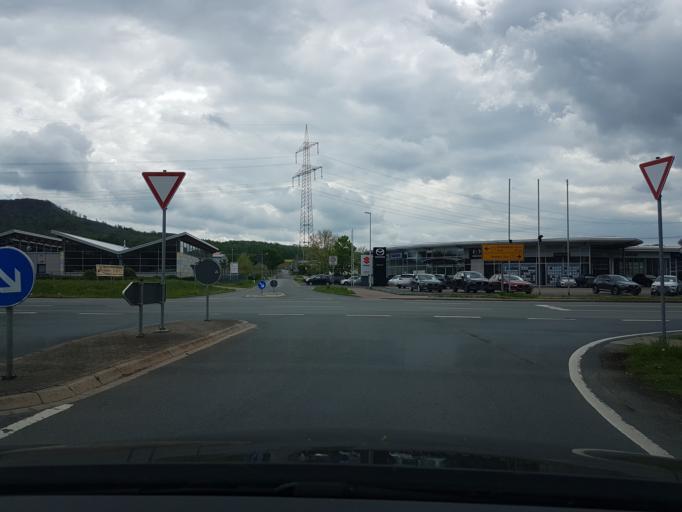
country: DE
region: Lower Saxony
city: Hameln
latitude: 52.1011
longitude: 9.4182
